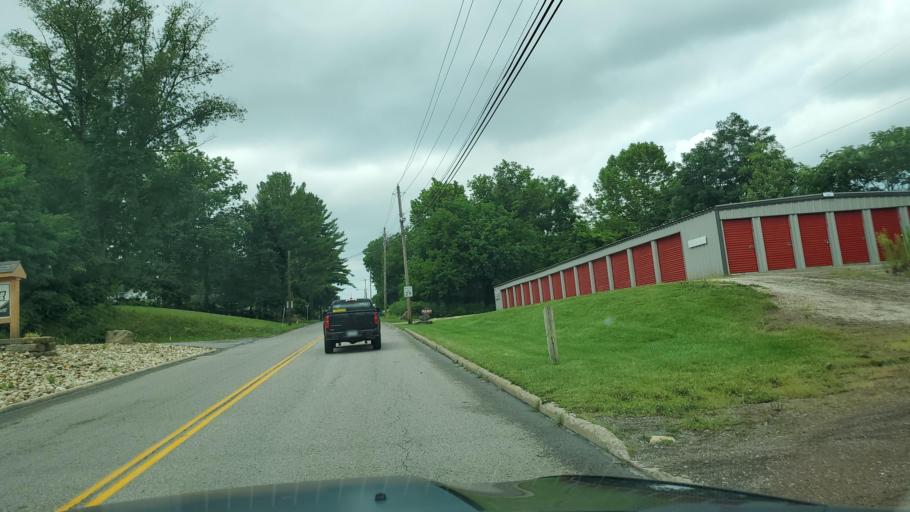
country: US
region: Ohio
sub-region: Mahoning County
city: Struthers
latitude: 41.0501
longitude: -80.5780
